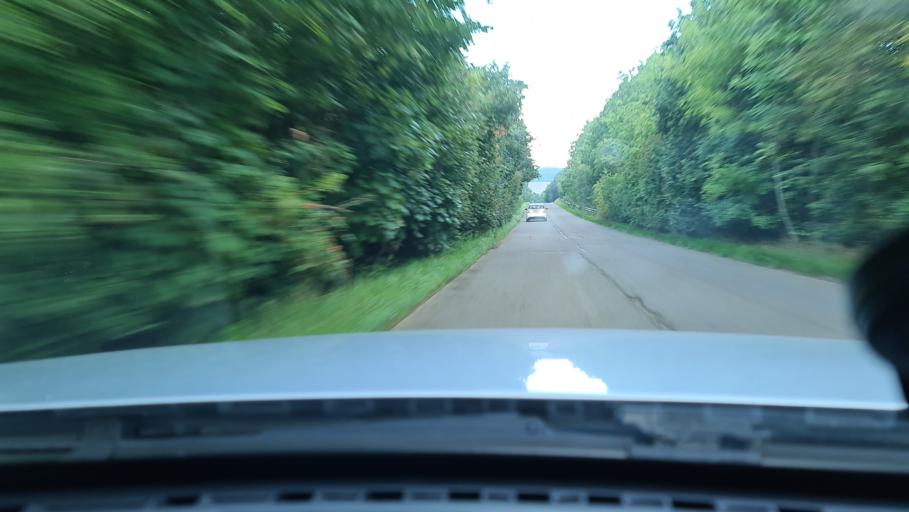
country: GB
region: England
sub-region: Oxfordshire
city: Hanwell
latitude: 52.0986
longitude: -1.3486
